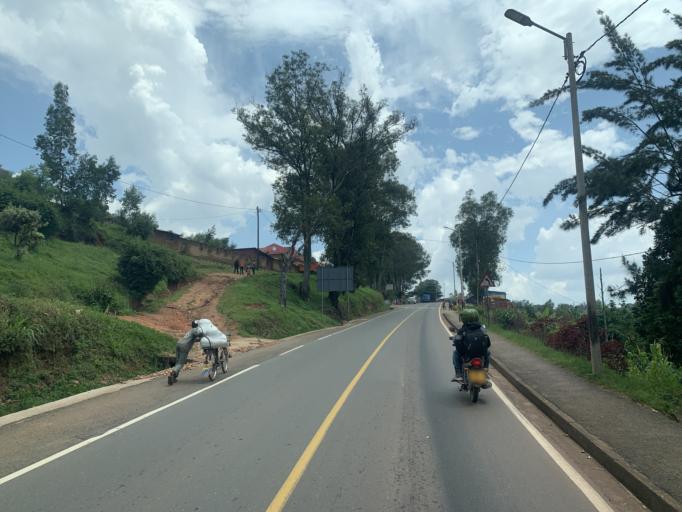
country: RW
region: Southern Province
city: Gitarama
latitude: -2.0016
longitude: 29.9032
